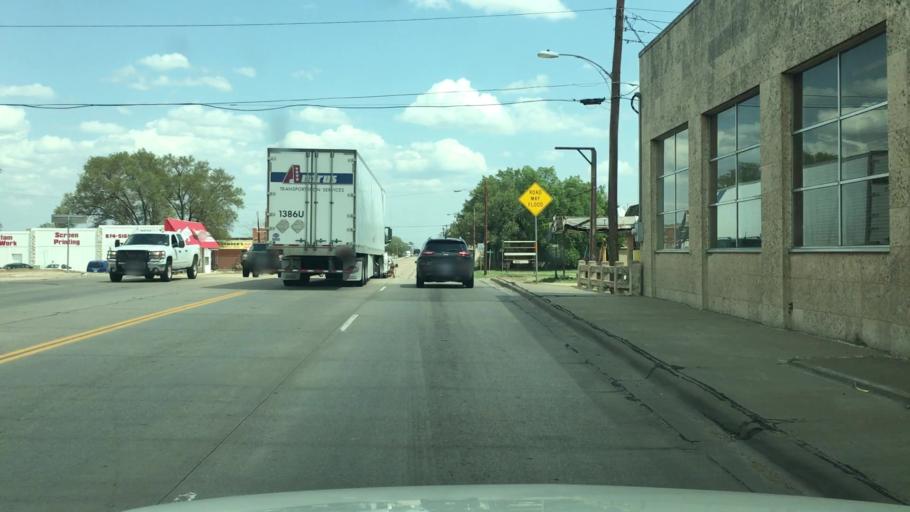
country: US
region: Texas
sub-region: Donley County
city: Clarendon
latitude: 34.9379
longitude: -100.8879
